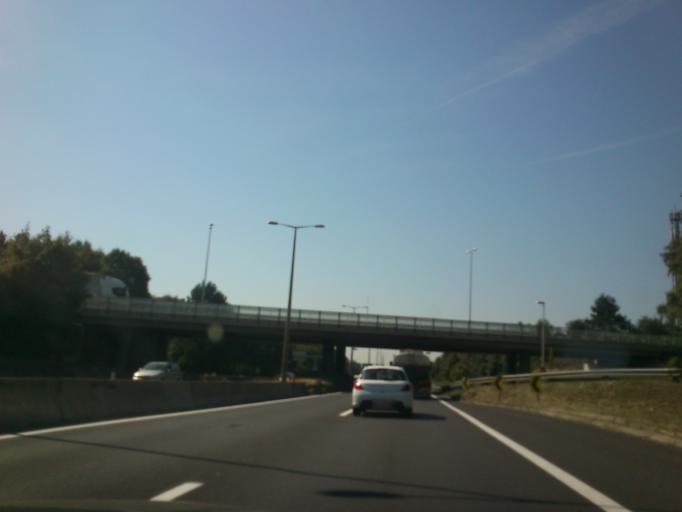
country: AT
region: Upper Austria
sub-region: Linz Stadt
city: Linz
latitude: 48.2608
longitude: 14.2970
